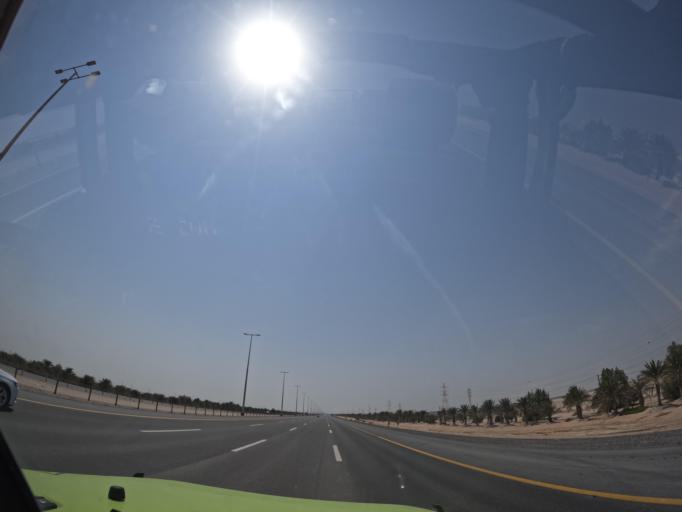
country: AE
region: Abu Dhabi
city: Abu Dhabi
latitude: 24.1948
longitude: 54.3903
